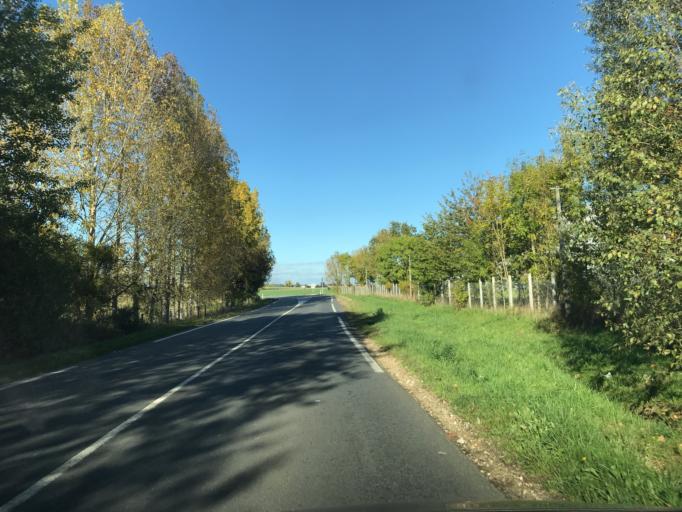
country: FR
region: Haute-Normandie
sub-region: Departement de l'Eure
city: Saint-Aubin-sur-Gaillon
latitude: 49.1250
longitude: 1.3108
